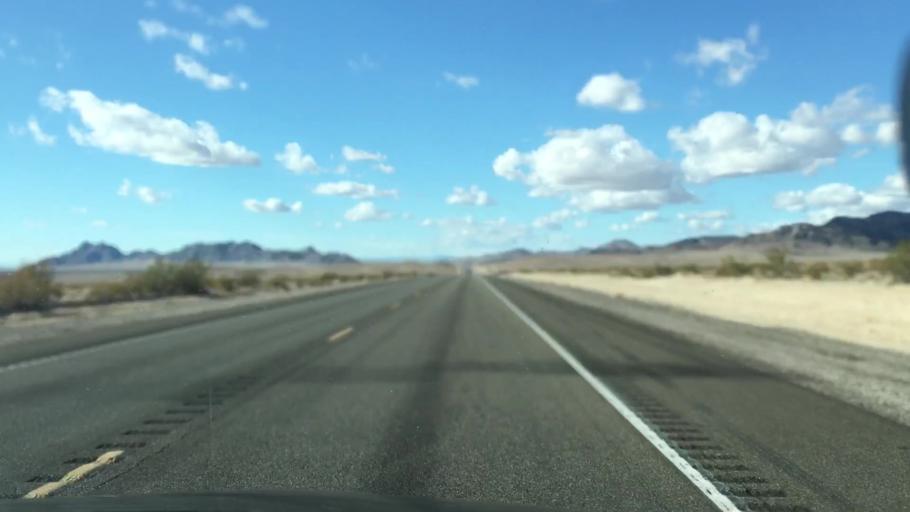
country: US
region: Nevada
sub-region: Nye County
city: Pahrump
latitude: 36.6021
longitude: -116.2509
